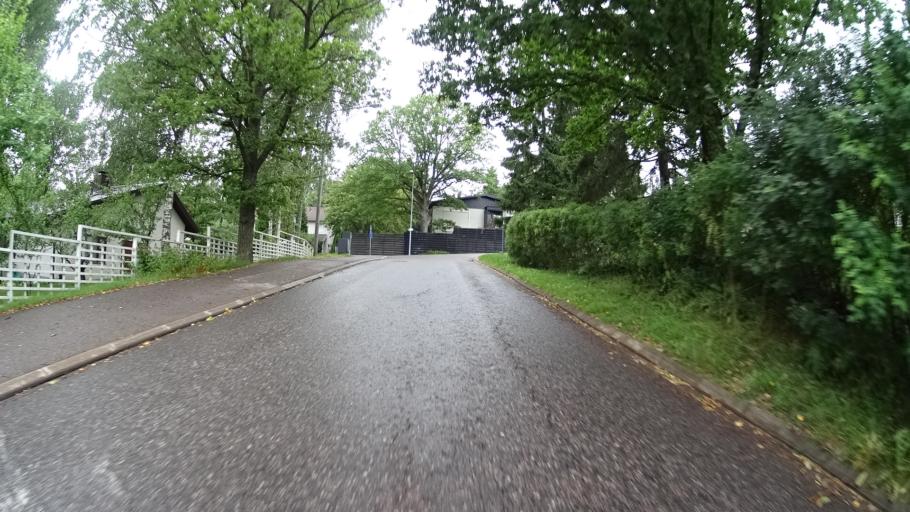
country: FI
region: Uusimaa
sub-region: Helsinki
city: Kauniainen
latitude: 60.2355
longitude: 24.7521
